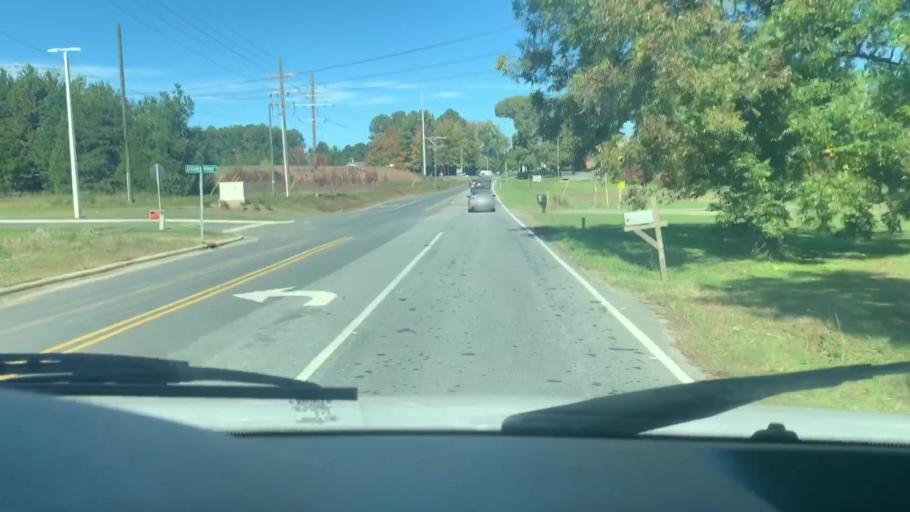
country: US
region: North Carolina
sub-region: Lincoln County
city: Lowesville
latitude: 35.4484
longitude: -80.9900
